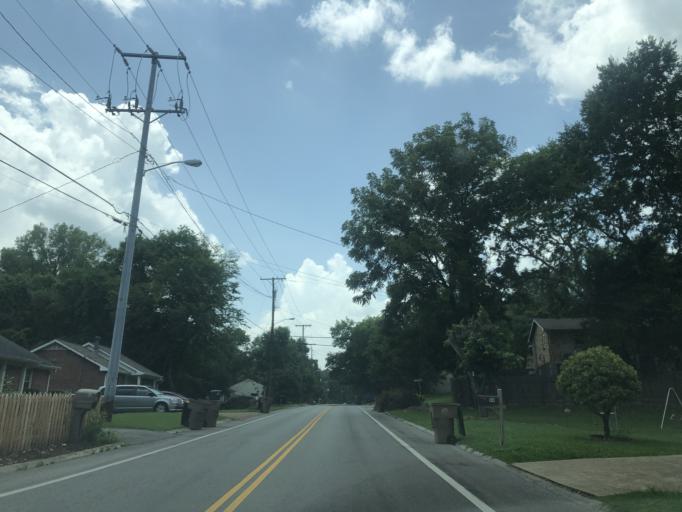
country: US
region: Tennessee
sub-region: Williamson County
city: Brentwood Estates
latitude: 36.0514
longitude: -86.6892
